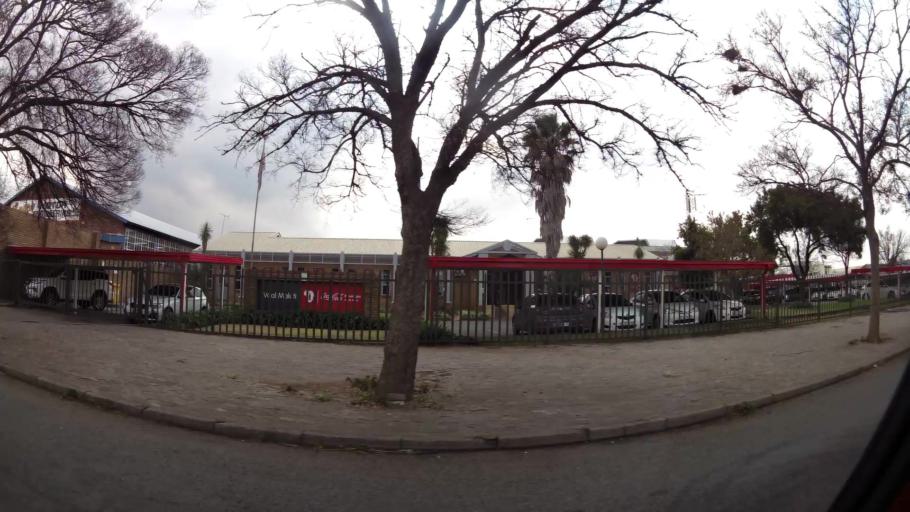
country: ZA
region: Gauteng
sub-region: Sedibeng District Municipality
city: Vanderbijlpark
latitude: -26.7053
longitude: 27.8483
